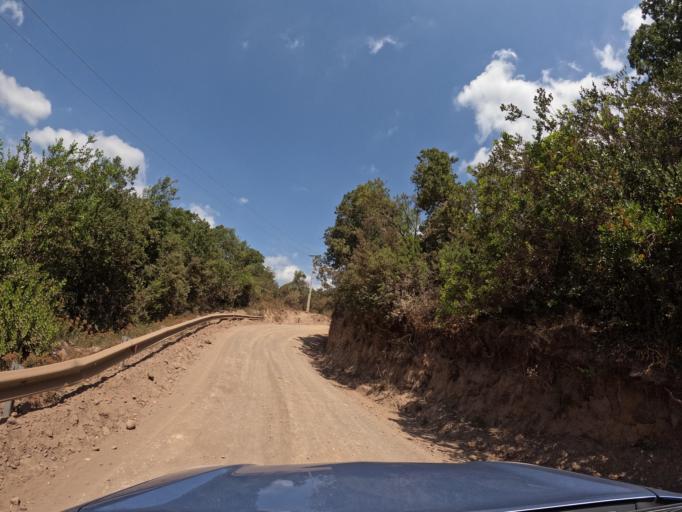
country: CL
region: Maule
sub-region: Provincia de Curico
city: Curico
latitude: -35.1202
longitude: -71.0072
